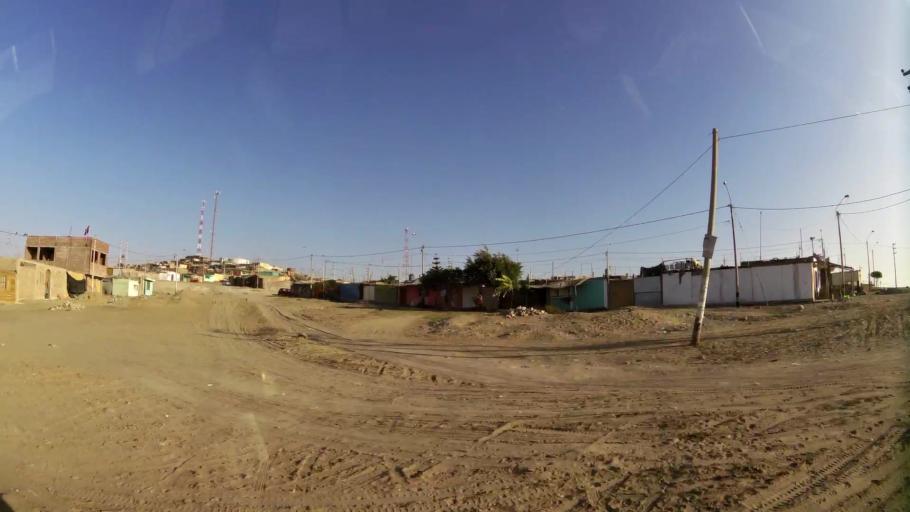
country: PE
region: Ica
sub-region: Provincia de Pisco
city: Villa Tupac Amaru
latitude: -13.7095
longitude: -76.1448
